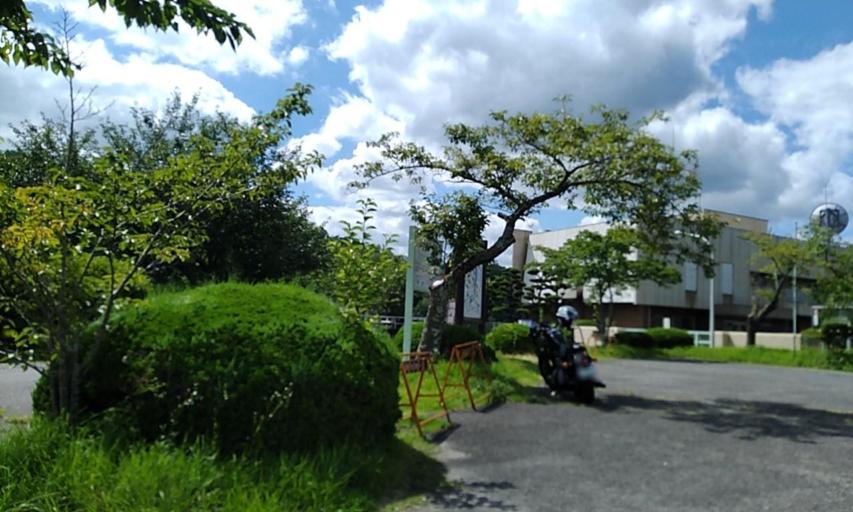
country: JP
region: Mie
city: Ueno-ebisumachi
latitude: 34.7528
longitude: 136.0131
